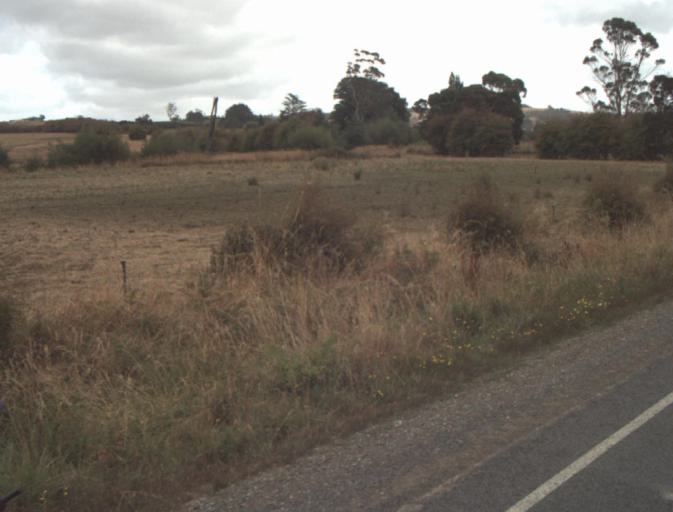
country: AU
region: Tasmania
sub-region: Launceston
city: Mayfield
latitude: -41.2444
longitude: 147.2169
